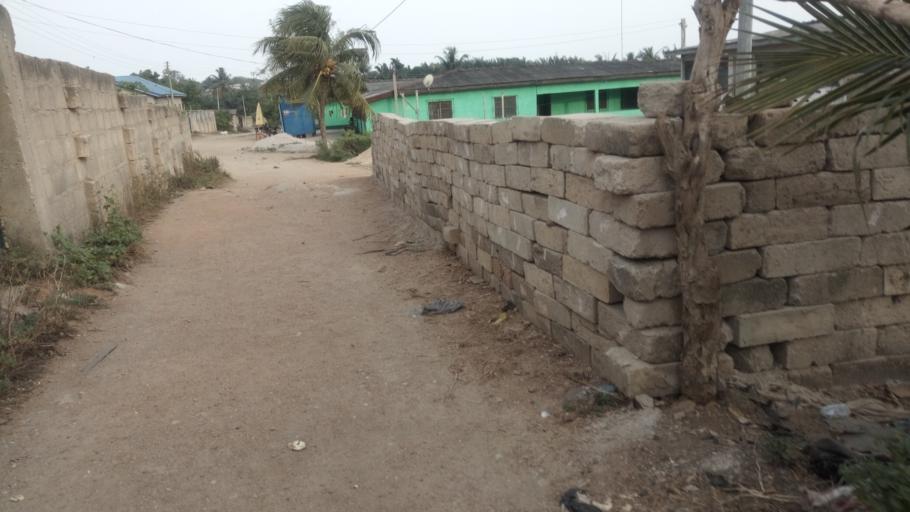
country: GH
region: Central
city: Winneba
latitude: 5.3556
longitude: -0.6246
